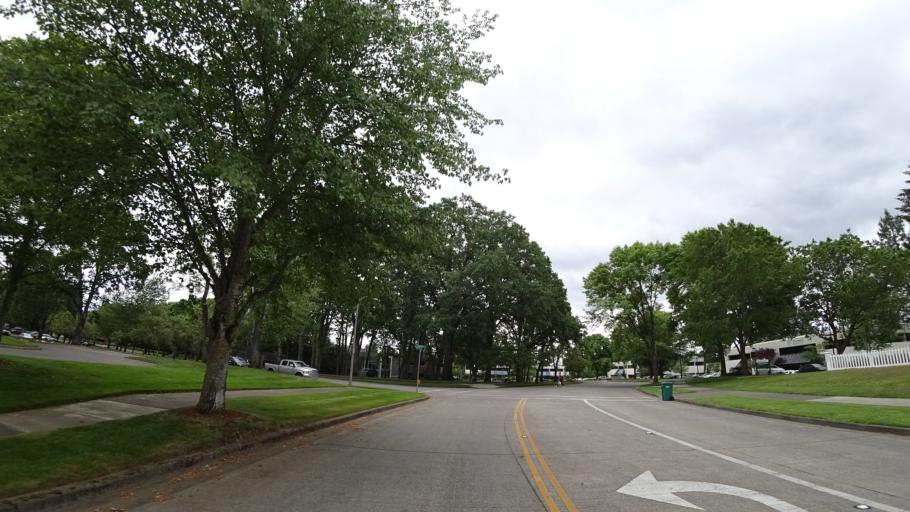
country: US
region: Oregon
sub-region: Washington County
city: Beaverton
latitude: 45.4589
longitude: -122.7927
